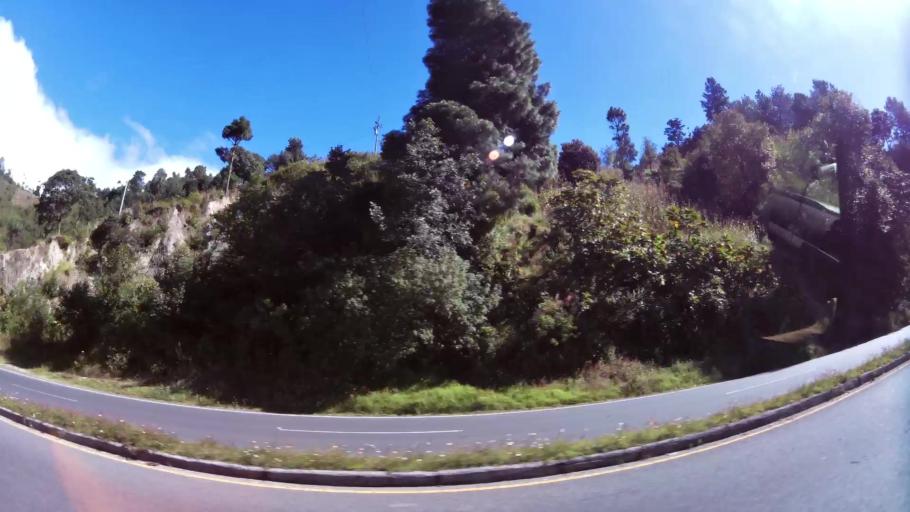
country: GT
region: Solola
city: Solola
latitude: 14.8294
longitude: -91.1885
